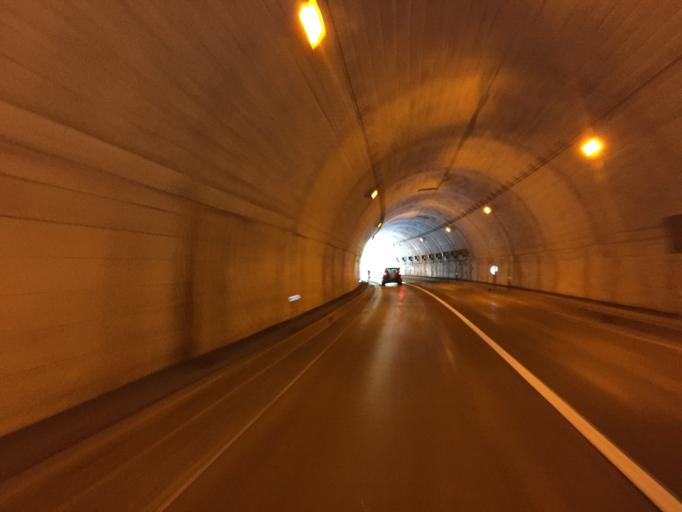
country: JP
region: Fukushima
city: Kitakata
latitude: 37.7810
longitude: 139.9276
